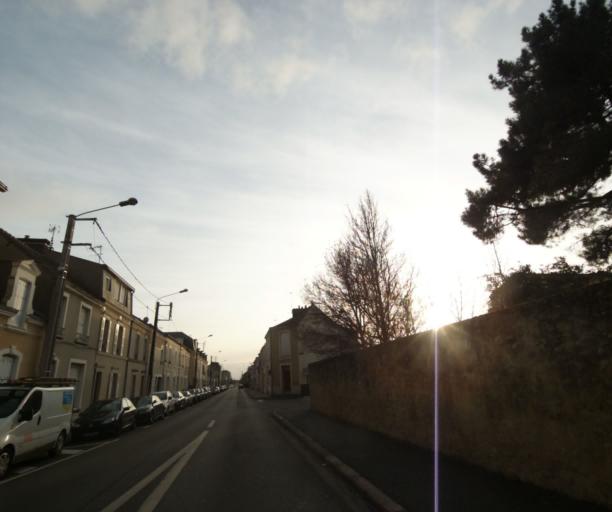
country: FR
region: Pays de la Loire
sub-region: Departement de la Sarthe
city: Le Mans
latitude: 48.0104
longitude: 0.1814
